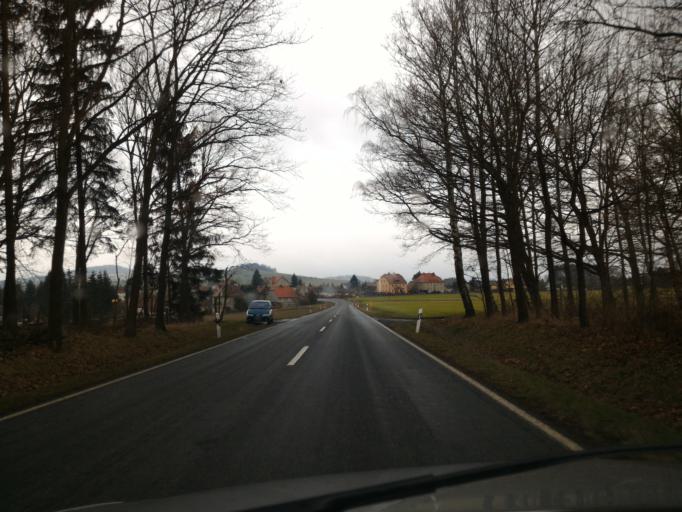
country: DE
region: Saxony
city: Leutersdorf
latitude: 50.9502
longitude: 14.6789
